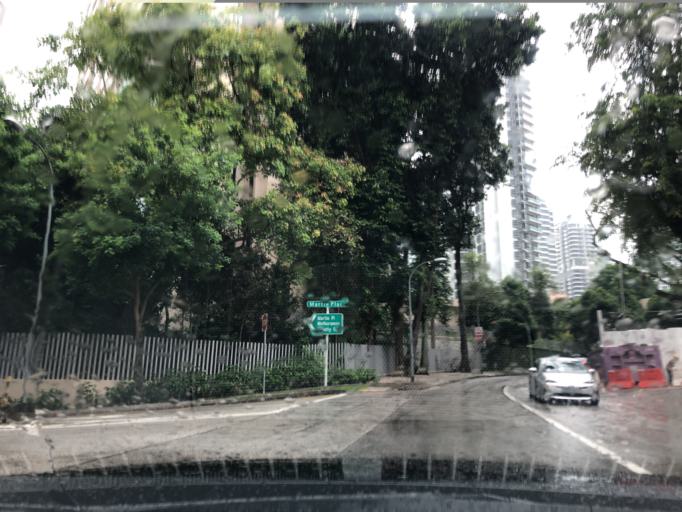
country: SG
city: Singapore
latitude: 1.2939
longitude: 103.8390
